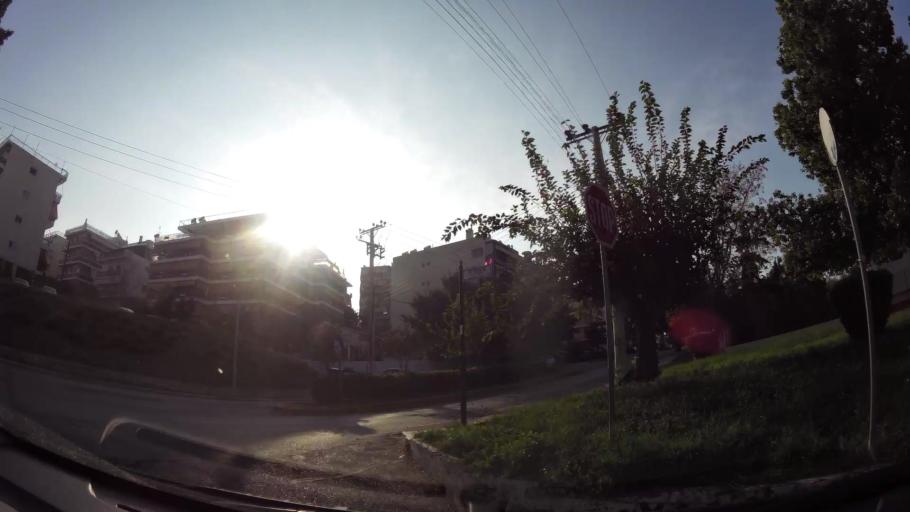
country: GR
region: Attica
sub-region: Nomarchia Athinas
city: Ilioupoli
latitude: 37.9347
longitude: 23.7515
